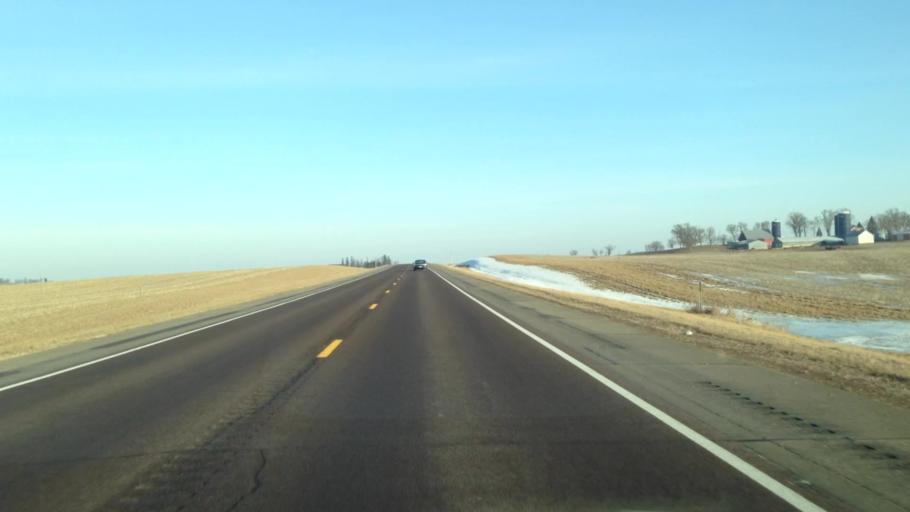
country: US
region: Minnesota
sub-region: Goodhue County
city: Goodhue
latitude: 44.4057
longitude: -92.6212
